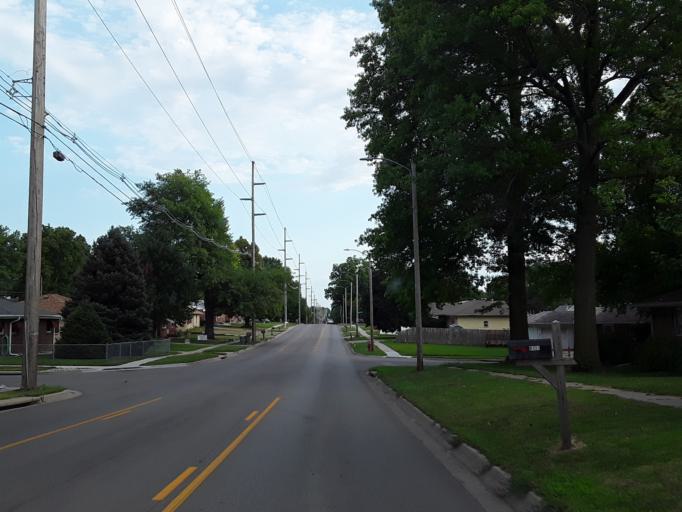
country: US
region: Nebraska
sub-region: Lancaster County
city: Lincoln
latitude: 40.8339
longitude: -96.6442
